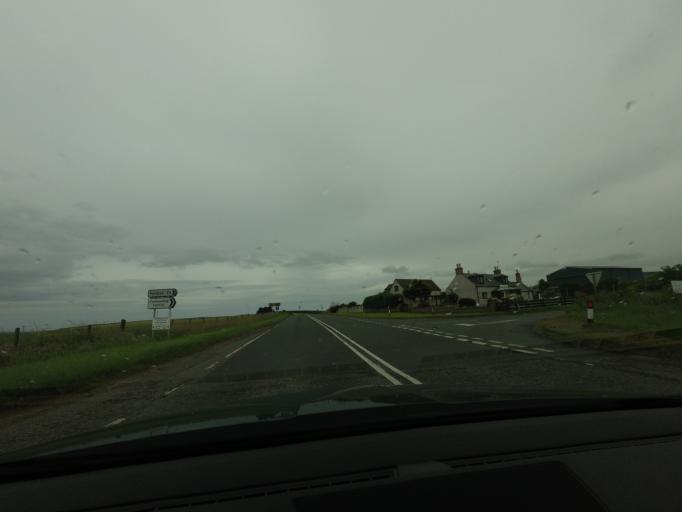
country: GB
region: Scotland
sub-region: Aberdeenshire
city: Portsoy
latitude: 57.6779
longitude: -2.7477
